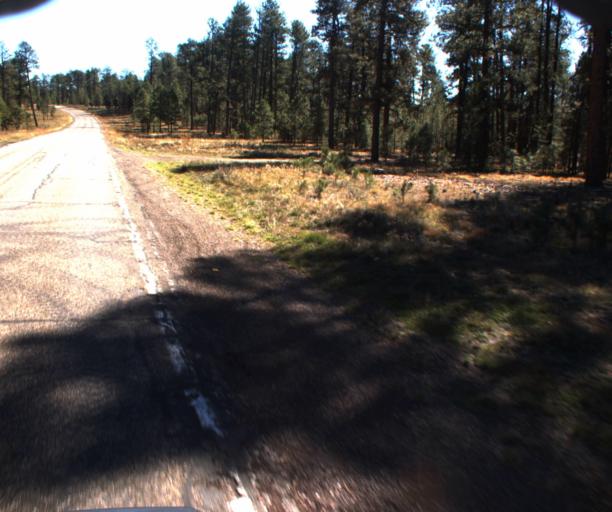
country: US
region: Arizona
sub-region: Coconino County
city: Fredonia
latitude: 36.7488
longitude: -112.2616
